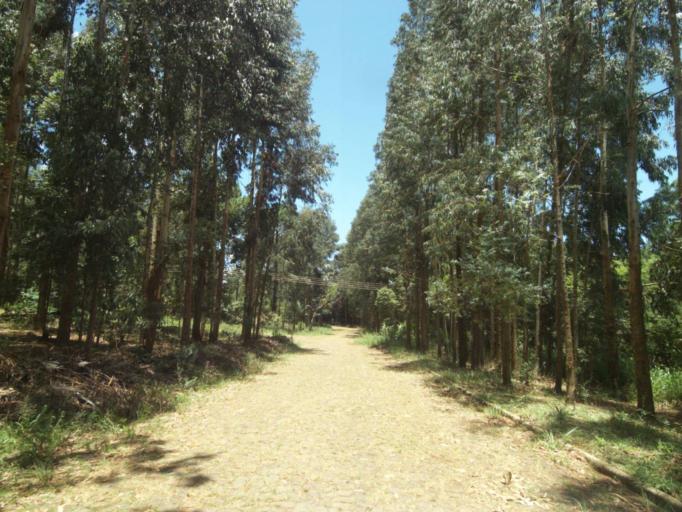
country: BR
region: Parana
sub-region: Pinhao
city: Pinhao
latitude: -25.7890
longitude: -52.0876
